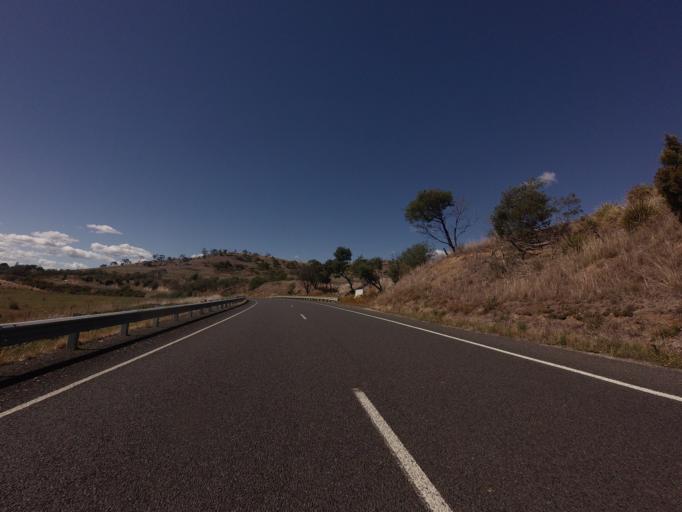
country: AU
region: Tasmania
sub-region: Break O'Day
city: St Helens
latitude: -41.7283
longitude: 147.8240
